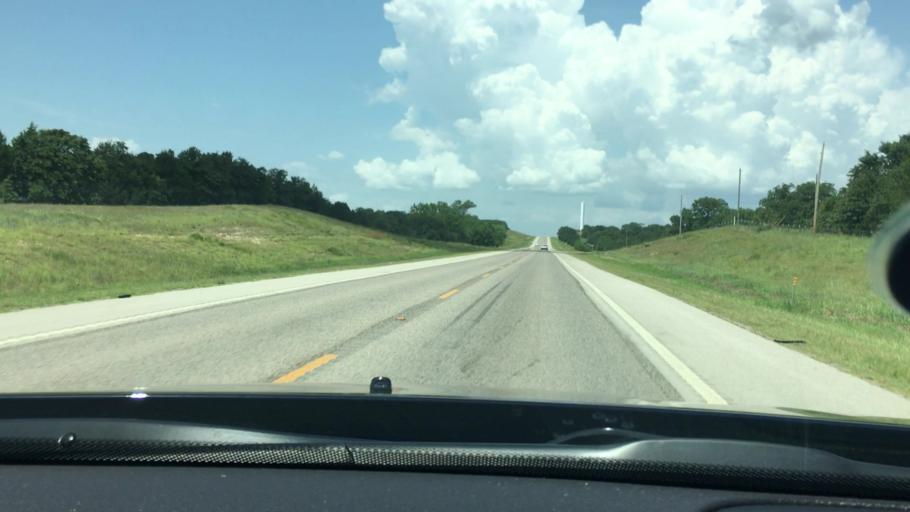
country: US
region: Oklahoma
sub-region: Carter County
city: Dickson
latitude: 34.1003
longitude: -96.9412
